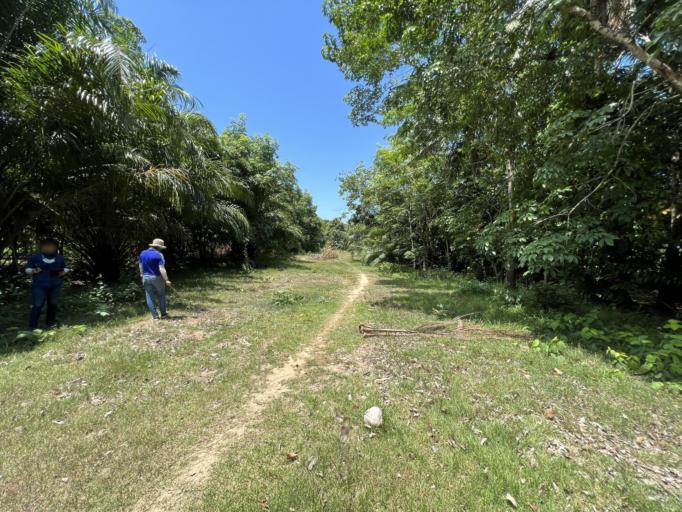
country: MM
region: Tanintharyi
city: Dawei
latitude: 14.5824
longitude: 97.9331
